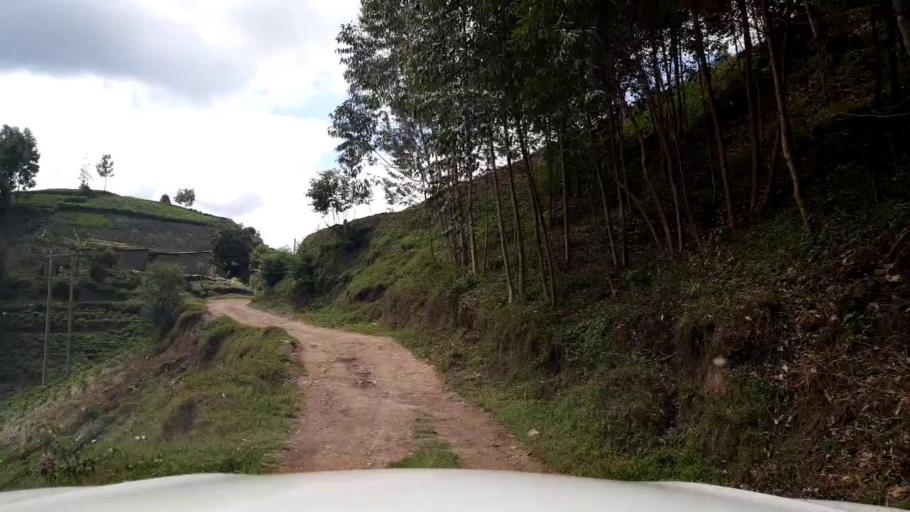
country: RW
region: Northern Province
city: Byumba
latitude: -1.5192
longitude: 30.1281
